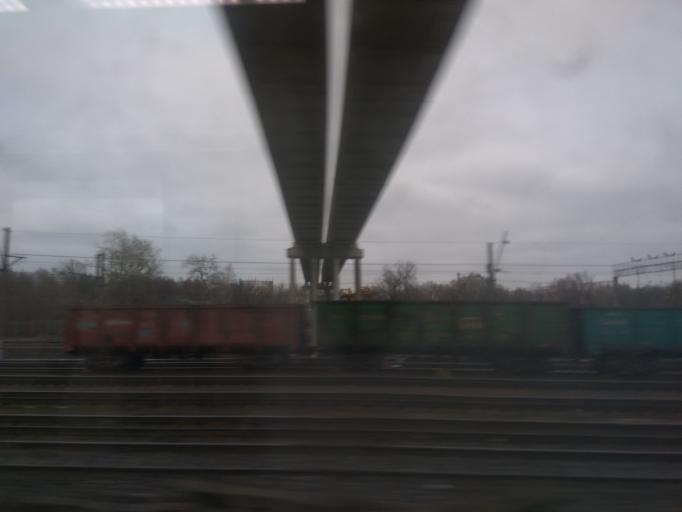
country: RU
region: Moscow
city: Lyublino
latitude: 55.6812
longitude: 37.7323
